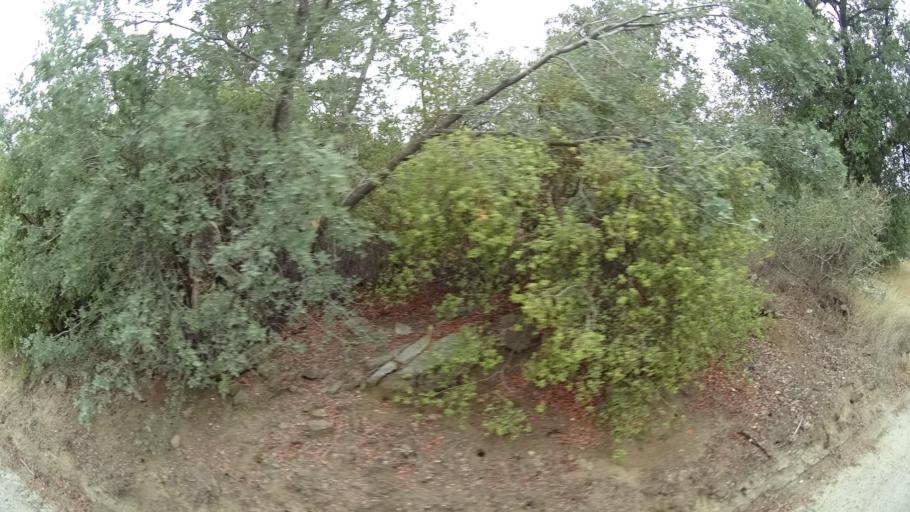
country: US
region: California
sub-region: San Diego County
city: Julian
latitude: 33.0017
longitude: -116.6440
